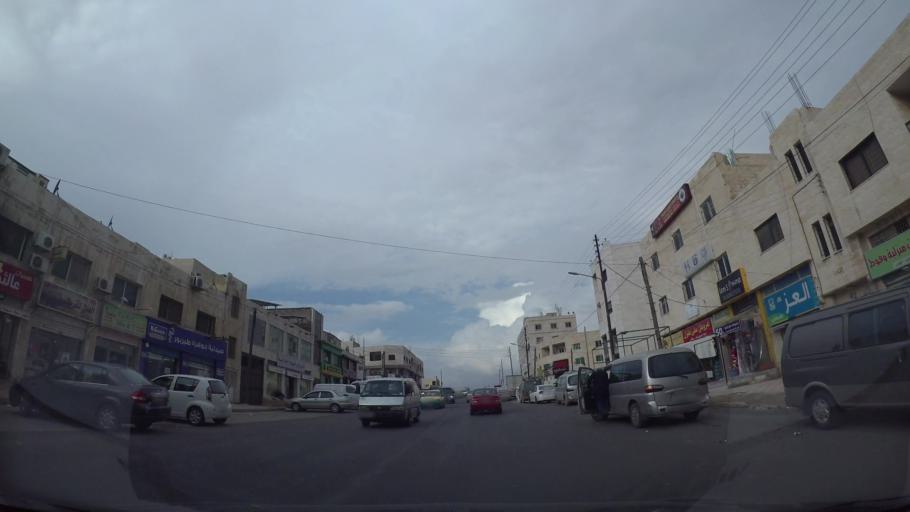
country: JO
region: Amman
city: Amman
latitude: 32.0028
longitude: 35.9494
